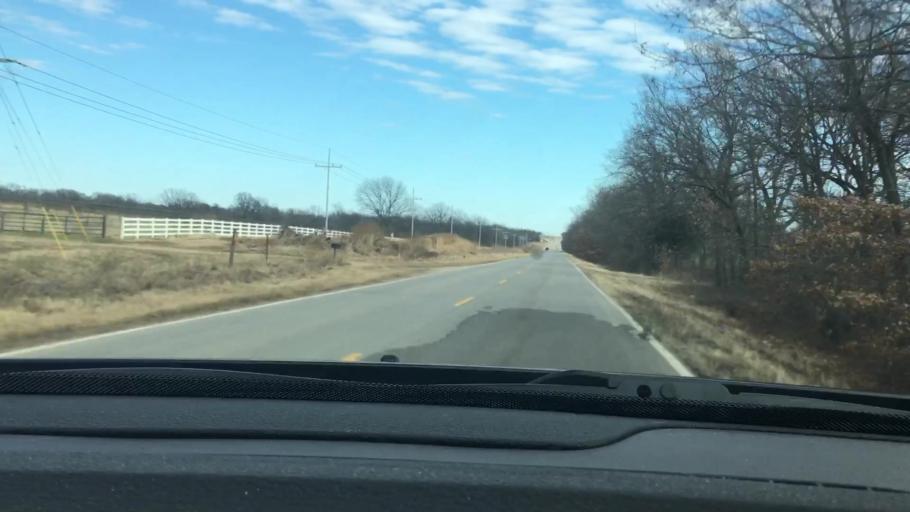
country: US
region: Oklahoma
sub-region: Garvin County
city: Stratford
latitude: 34.7967
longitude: -96.8755
